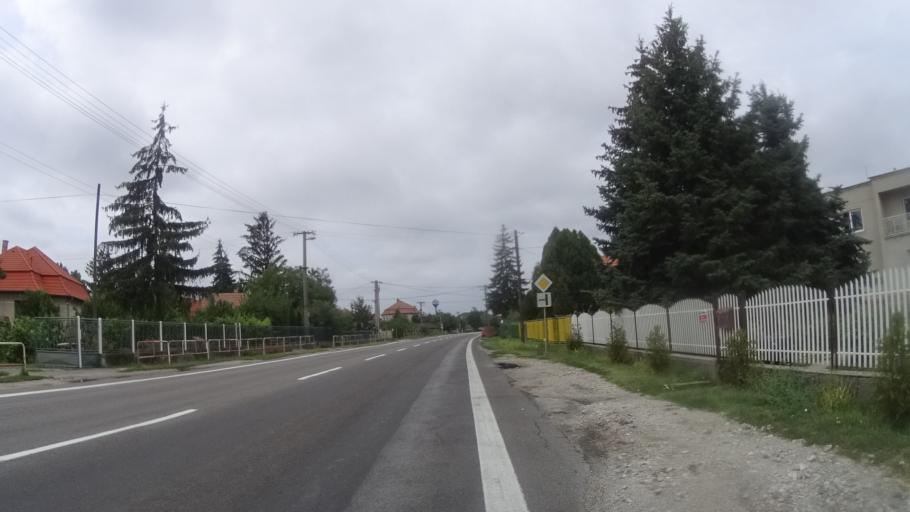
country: HU
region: Komarom-Esztergom
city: Acs
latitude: 47.7647
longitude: 18.0404
